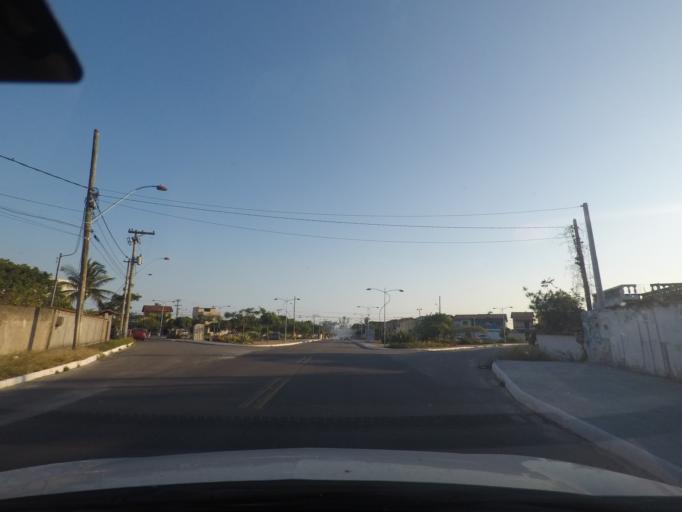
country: BR
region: Rio de Janeiro
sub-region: Marica
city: Marica
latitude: -22.9688
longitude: -42.9271
